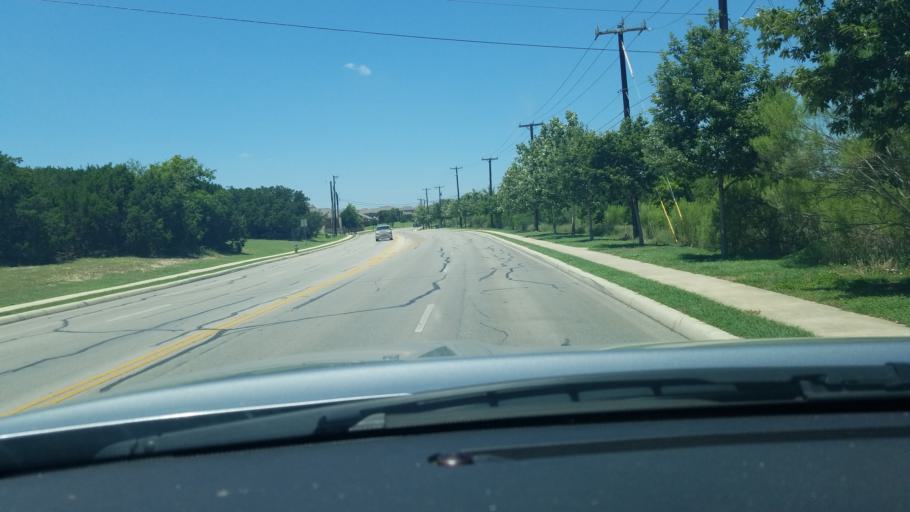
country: US
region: Texas
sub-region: Bexar County
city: Timberwood Park
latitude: 29.6938
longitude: -98.4794
